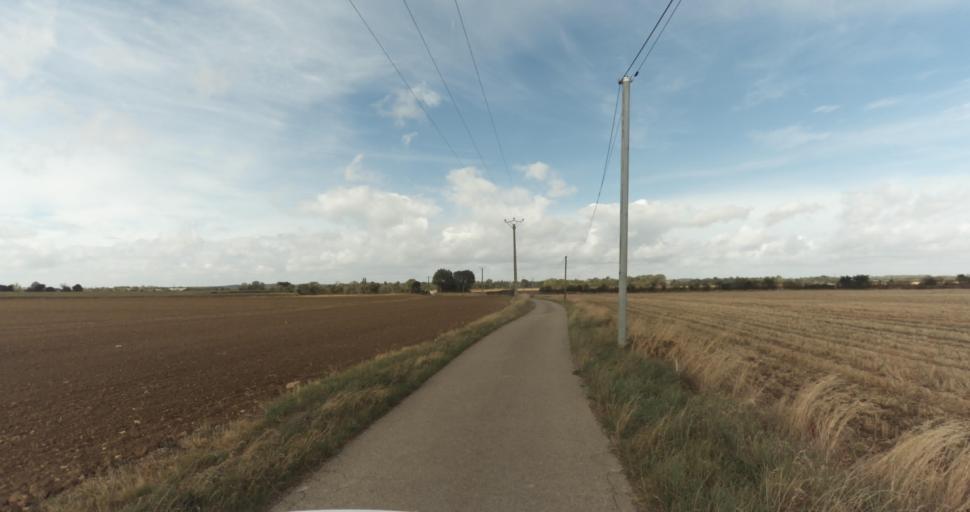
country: FR
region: Lower Normandy
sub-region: Departement de l'Orne
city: Sainte-Gauburge-Sainte-Colombe
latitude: 48.8237
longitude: 0.4046
